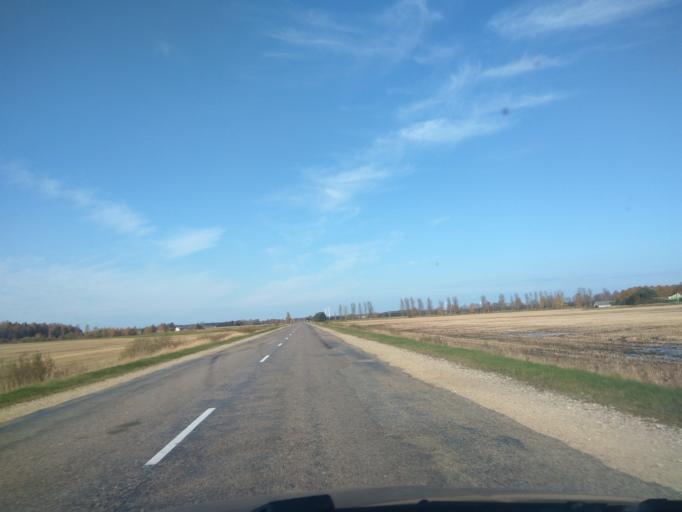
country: LV
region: Ventspils Rajons
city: Piltene
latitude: 57.2483
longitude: 21.5933
